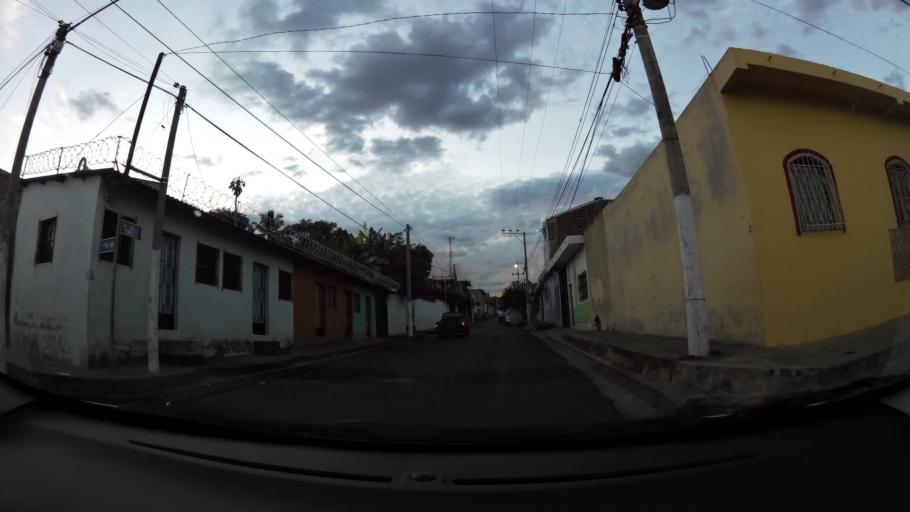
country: SV
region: San Vicente
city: San Vicente
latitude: 13.6407
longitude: -88.7866
